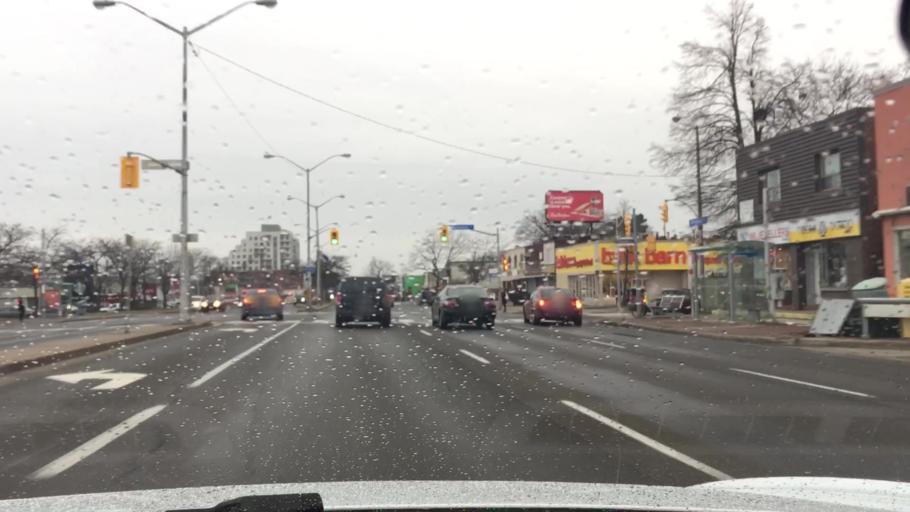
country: CA
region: Ontario
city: Scarborough
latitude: 43.7092
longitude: -79.2500
